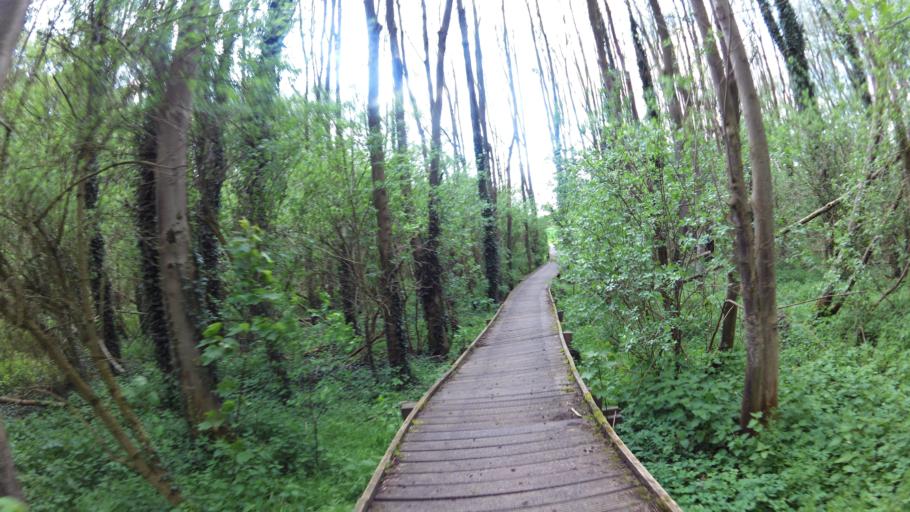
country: NL
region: Limburg
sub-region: Gemeente Kerkrade
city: Kerkrade
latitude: 50.8514
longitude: 6.0578
